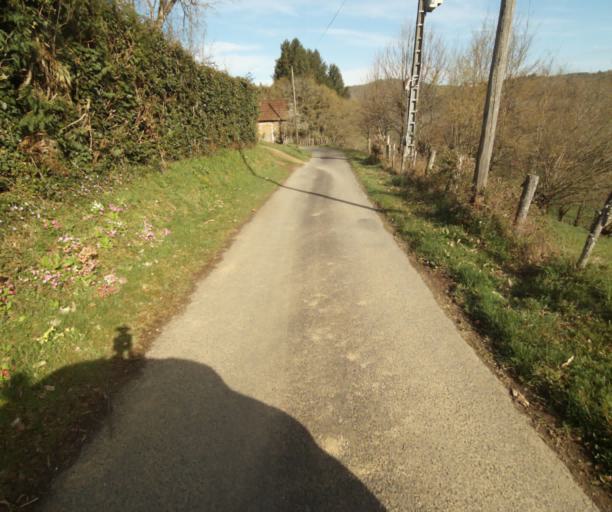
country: FR
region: Limousin
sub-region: Departement de la Correze
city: Naves
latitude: 45.3348
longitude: 1.8198
